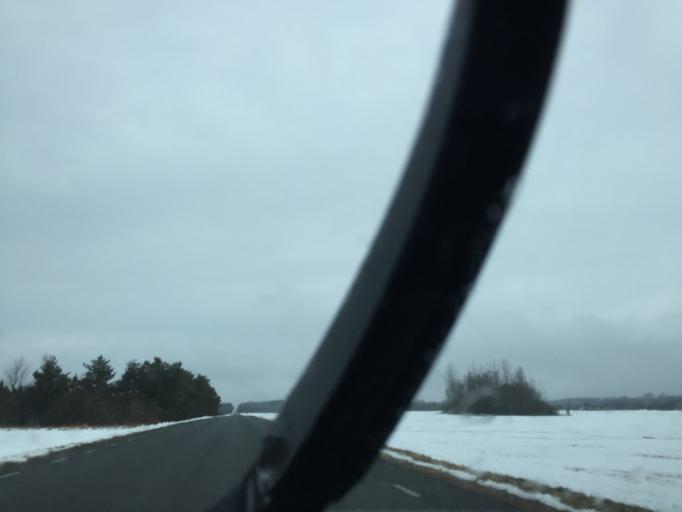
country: EE
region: Saare
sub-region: Kuressaare linn
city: Kuressaare
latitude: 58.3248
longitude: 22.0232
